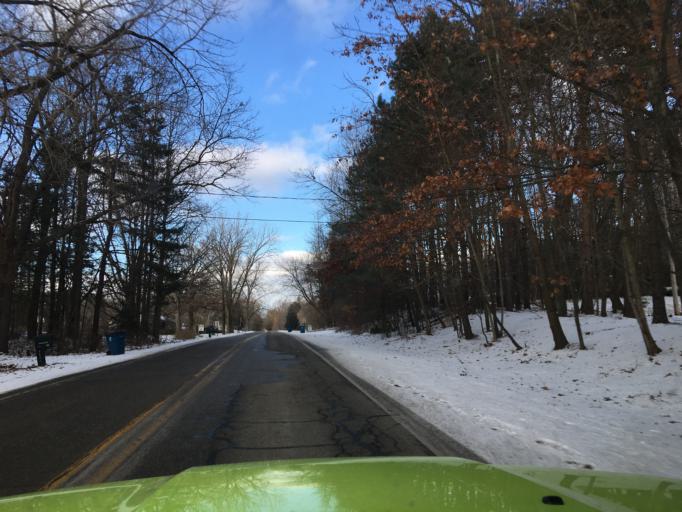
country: US
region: Michigan
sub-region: Montcalm County
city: Greenville
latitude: 43.1847
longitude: -85.2830
